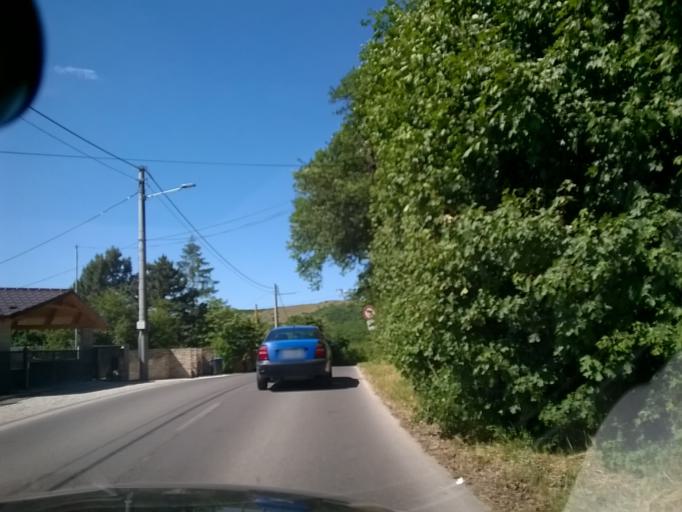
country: SK
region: Nitriansky
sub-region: Okres Nitra
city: Nitra
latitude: 48.3404
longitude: 18.0867
